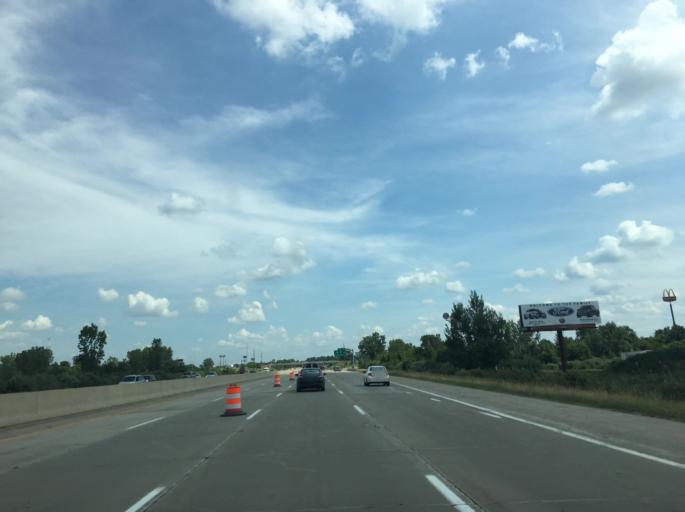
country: US
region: Michigan
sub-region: Saginaw County
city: Birch Run
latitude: 43.2548
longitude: -83.7801
